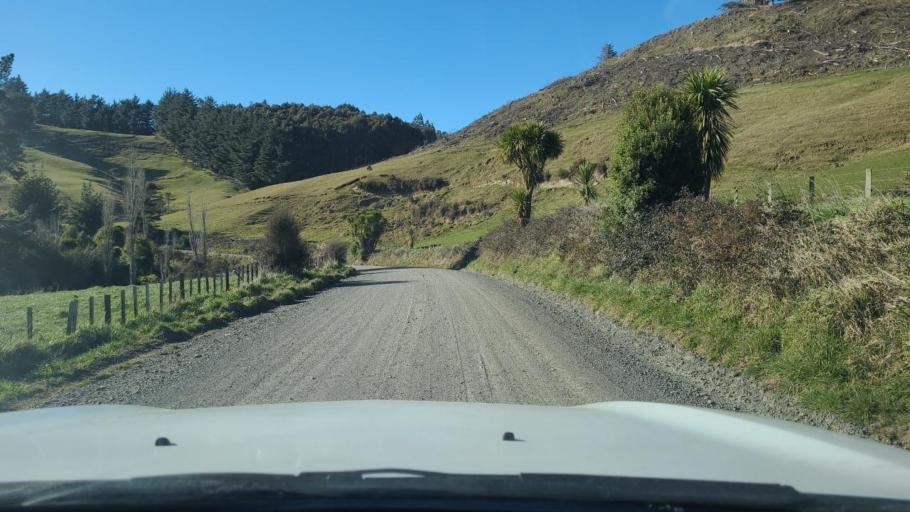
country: NZ
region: Hawke's Bay
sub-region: Napier City
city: Taradale
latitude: -39.3488
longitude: 176.5438
